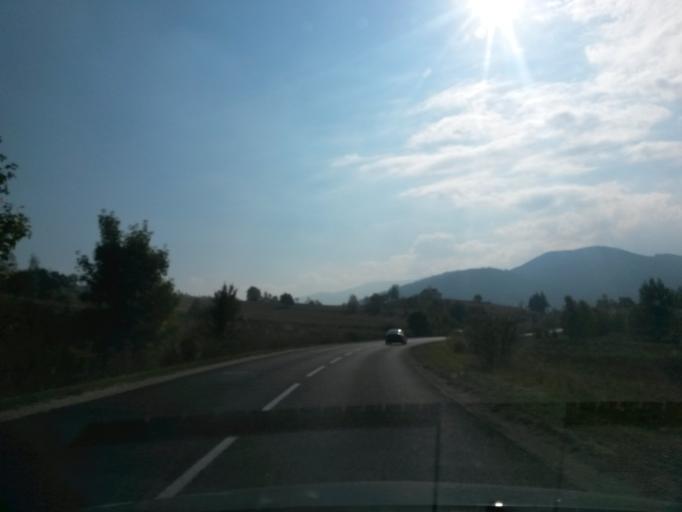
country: PL
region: Lower Silesian Voivodeship
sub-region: Powiat jeleniogorski
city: Sosnowka
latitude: 50.8311
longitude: 15.7204
